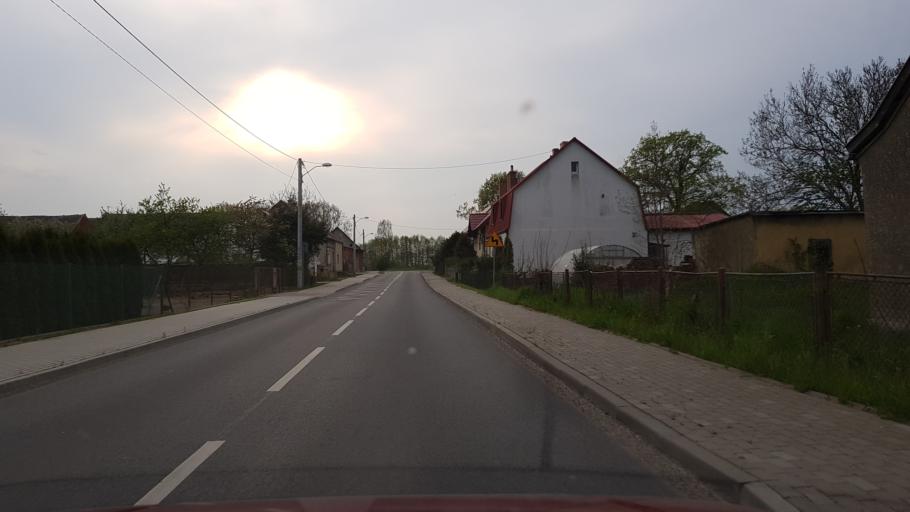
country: PL
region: West Pomeranian Voivodeship
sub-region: Powiat pyrzycki
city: Bielice
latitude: 53.2748
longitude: 14.6681
